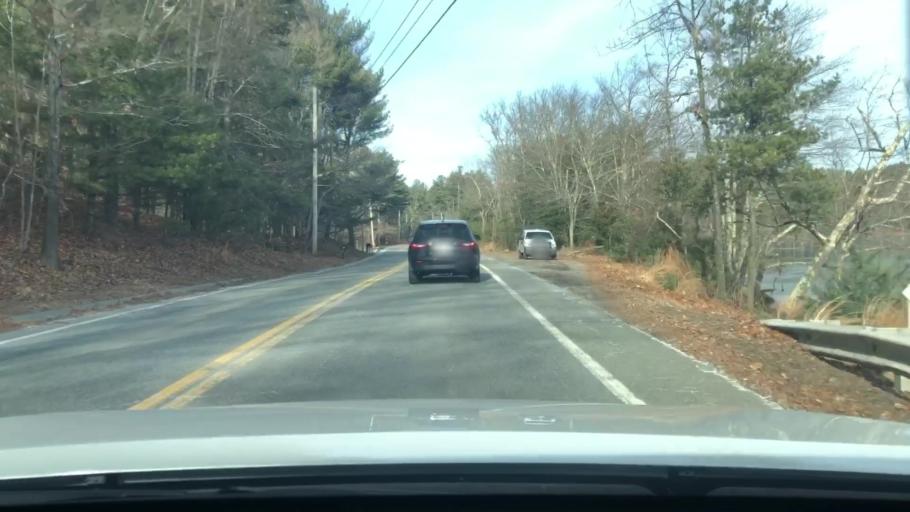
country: US
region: Massachusetts
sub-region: Worcester County
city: Grafton
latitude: 42.1918
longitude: -71.6566
